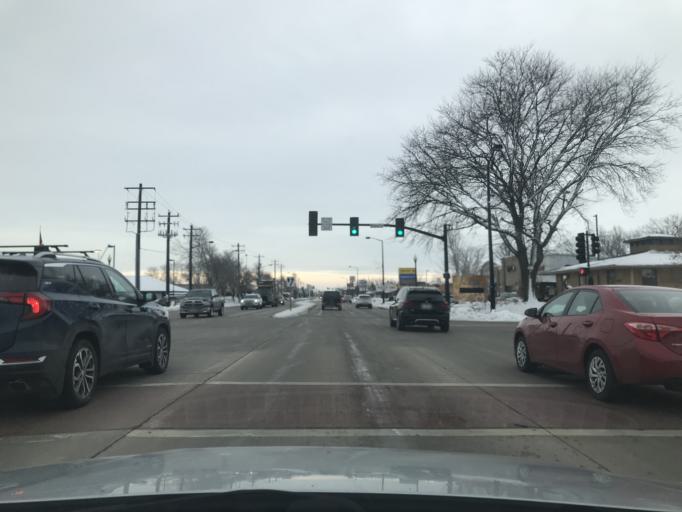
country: US
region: Wisconsin
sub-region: Brown County
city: Ashwaubenon
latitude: 44.4873
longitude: -88.0666
